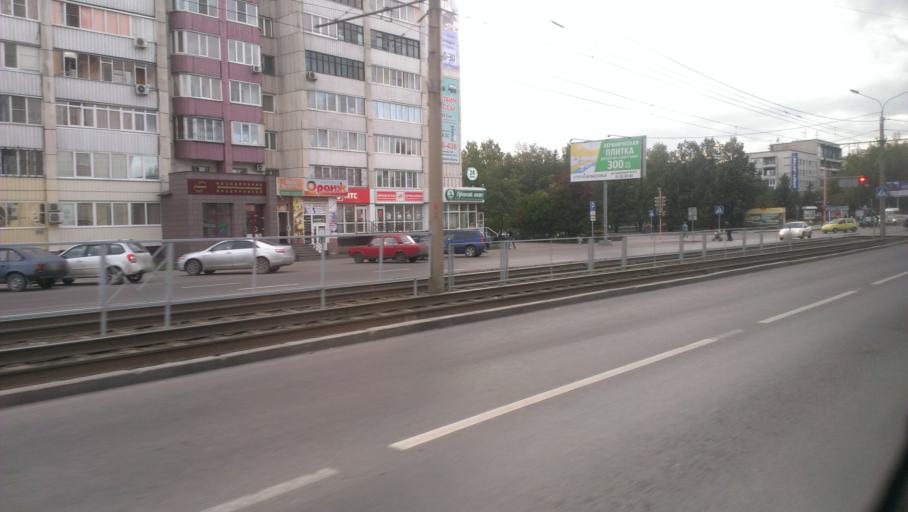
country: RU
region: Altai Krai
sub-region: Gorod Barnaulskiy
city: Barnaul
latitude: 53.3443
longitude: 83.7673
